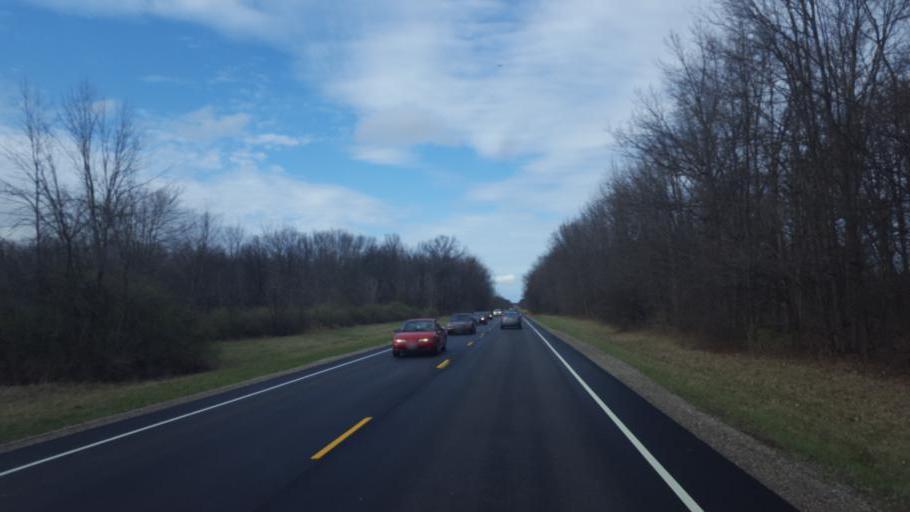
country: US
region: Ohio
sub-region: Franklin County
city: Westerville
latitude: 40.1854
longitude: -82.9110
